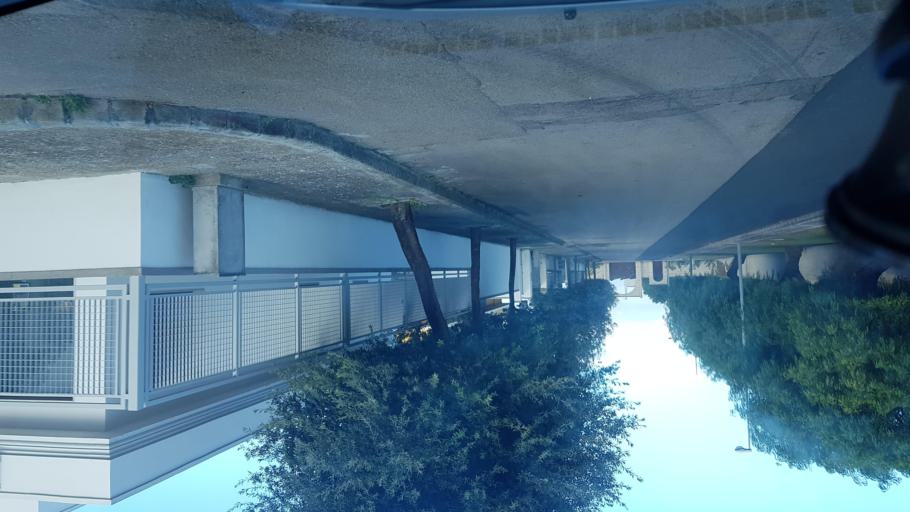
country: IT
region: Apulia
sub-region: Provincia di Lecce
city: Veglie
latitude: 40.3465
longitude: 17.9694
